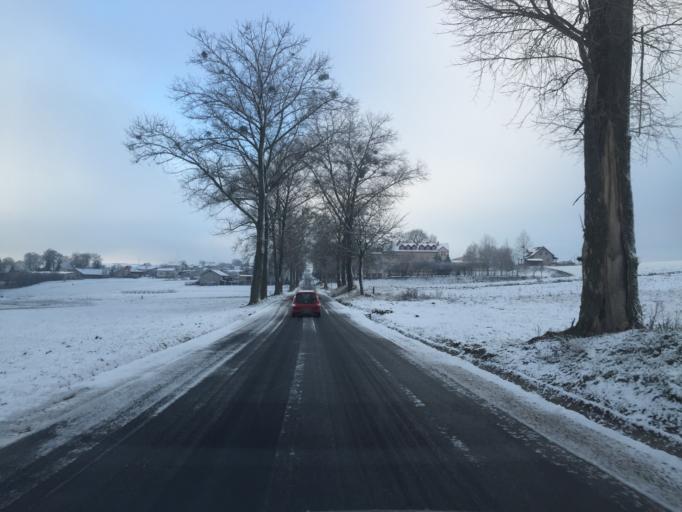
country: PL
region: Kujawsko-Pomorskie
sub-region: Powiat brodnicki
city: Bartniczka
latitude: 53.2559
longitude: 19.6444
